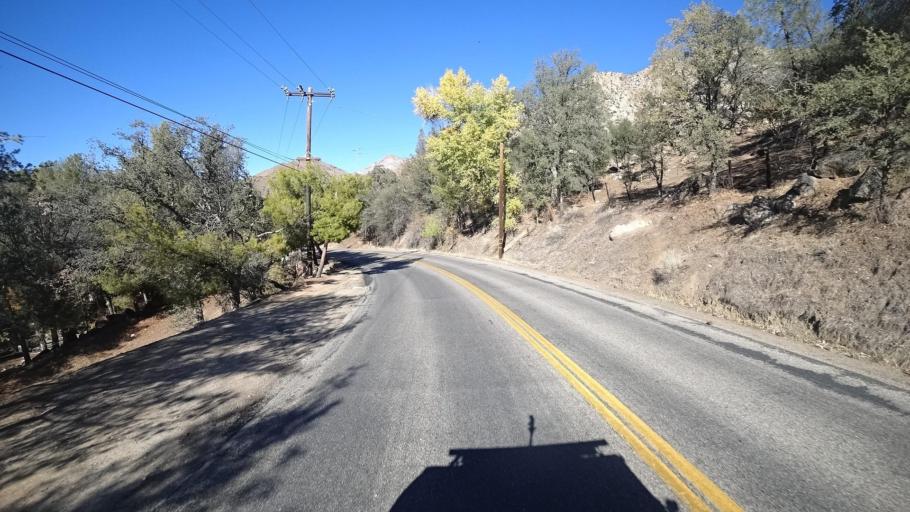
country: US
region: California
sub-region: Kern County
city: Kernville
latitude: 35.7606
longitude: -118.4202
